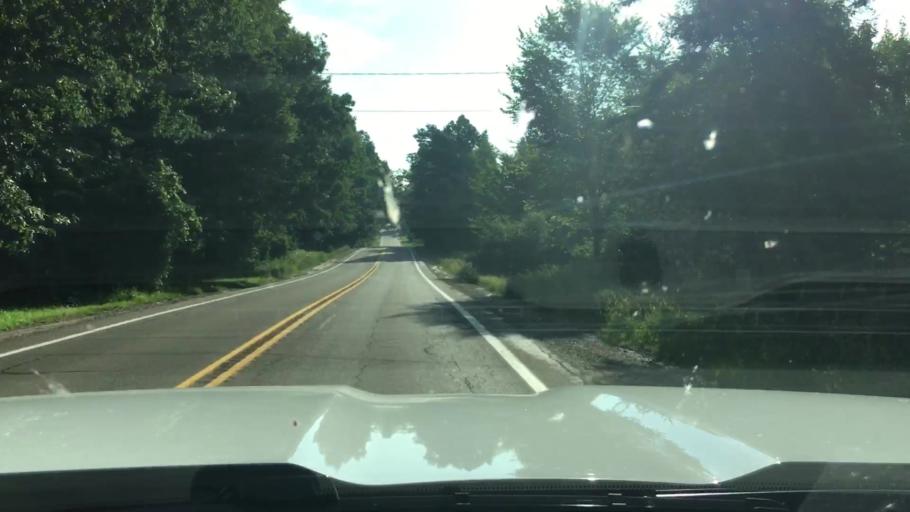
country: US
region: Michigan
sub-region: Kent County
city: Cedar Springs
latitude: 43.2194
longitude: -85.6338
